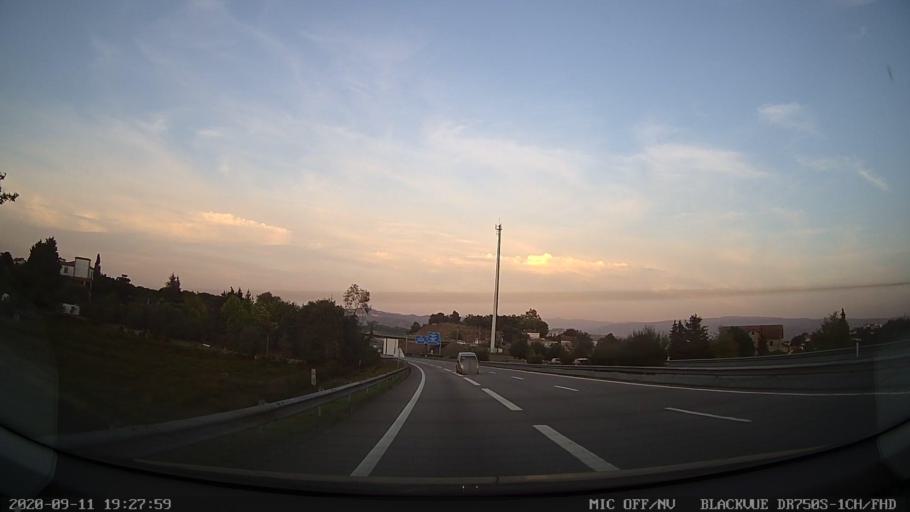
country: PT
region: Porto
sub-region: Lousada
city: Meinedo
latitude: 41.2306
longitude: -8.2110
